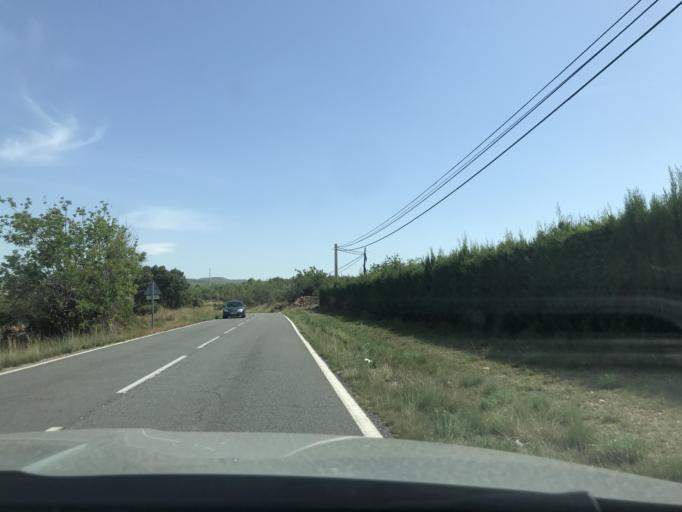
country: ES
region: Catalonia
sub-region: Provincia de Tarragona
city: Altafulla
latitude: 41.1716
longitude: 1.3700
